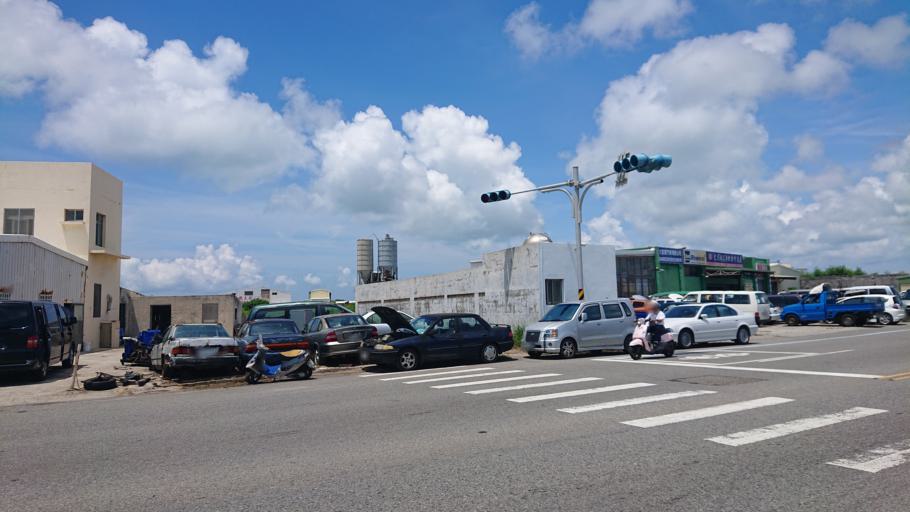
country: TW
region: Taiwan
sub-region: Penghu
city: Ma-kung
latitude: 23.5690
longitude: 119.5877
